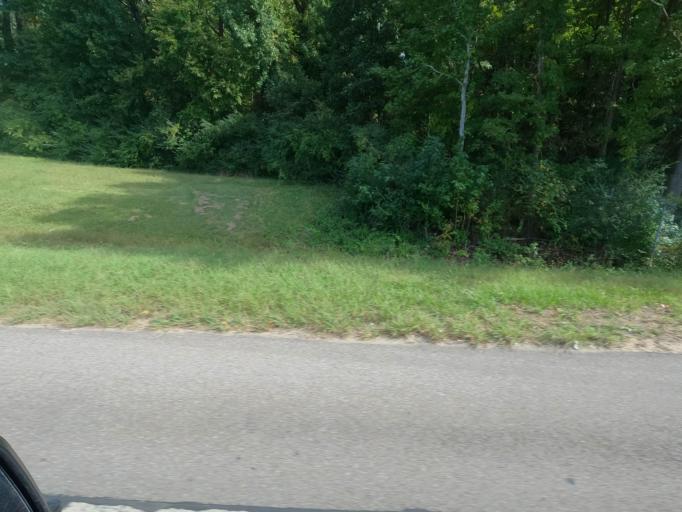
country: US
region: Tennessee
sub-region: Shelby County
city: Lakeland
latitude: 35.1949
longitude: -89.7897
